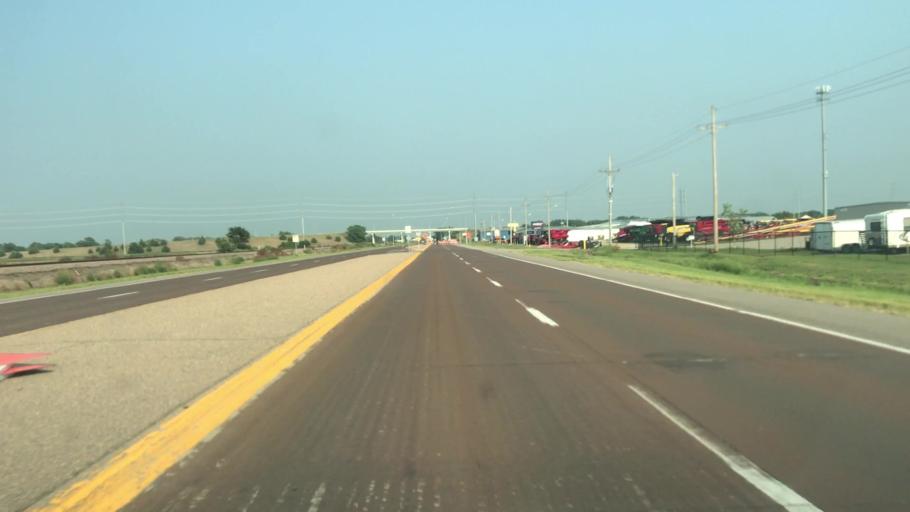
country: US
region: Nebraska
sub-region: Hall County
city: Grand Island
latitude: 40.9554
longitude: -98.3928
